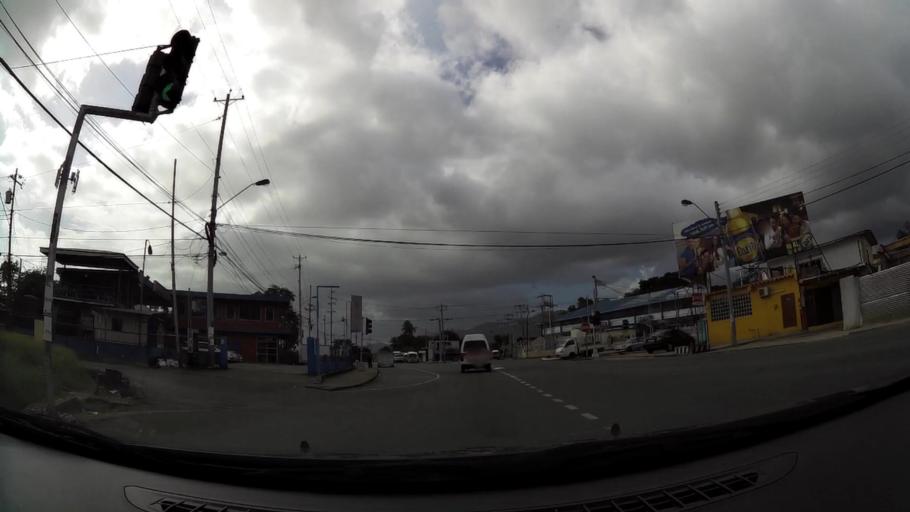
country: TT
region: Tunapuna/Piarco
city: Arouca
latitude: 10.6390
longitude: -61.3488
